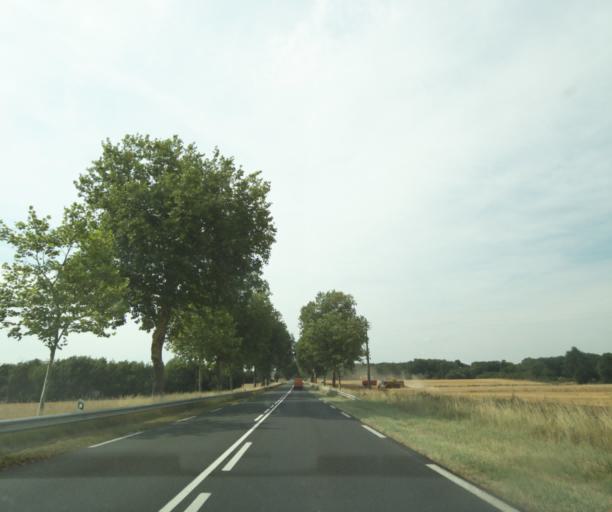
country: FR
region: Centre
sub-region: Departement d'Indre-et-Loire
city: Saint-Antoine-du-Rocher
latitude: 47.5163
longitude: 0.5872
